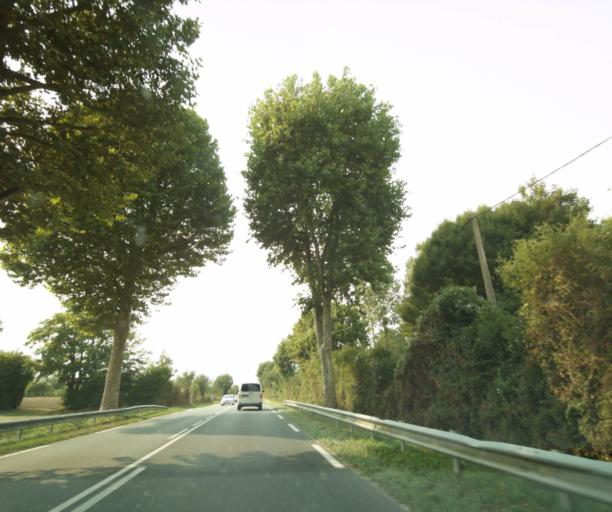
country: FR
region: Centre
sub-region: Departement de l'Indre
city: Chatillon-sur-Indre
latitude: 46.9713
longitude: 1.1930
